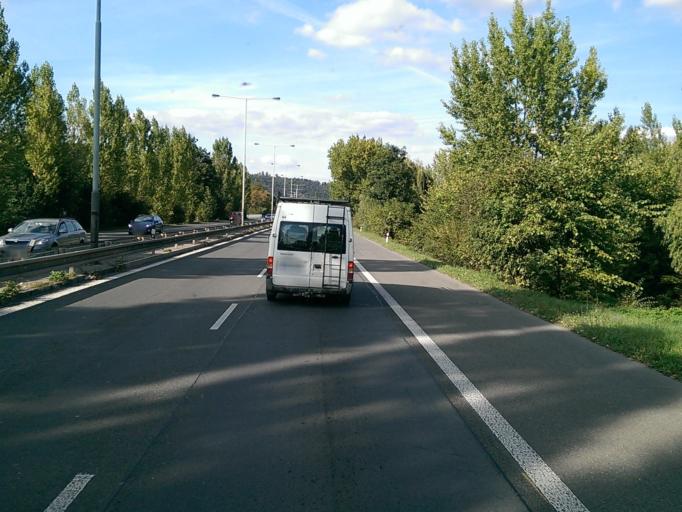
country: CZ
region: Praha
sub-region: Praha 12
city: Modrany
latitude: 50.0075
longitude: 14.3949
